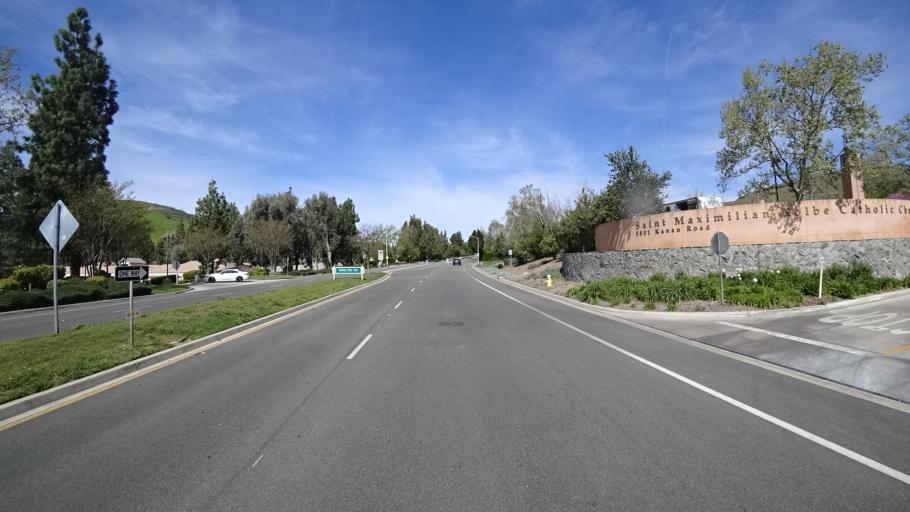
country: US
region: California
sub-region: Ventura County
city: Oak Park
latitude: 34.1853
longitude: -118.7868
